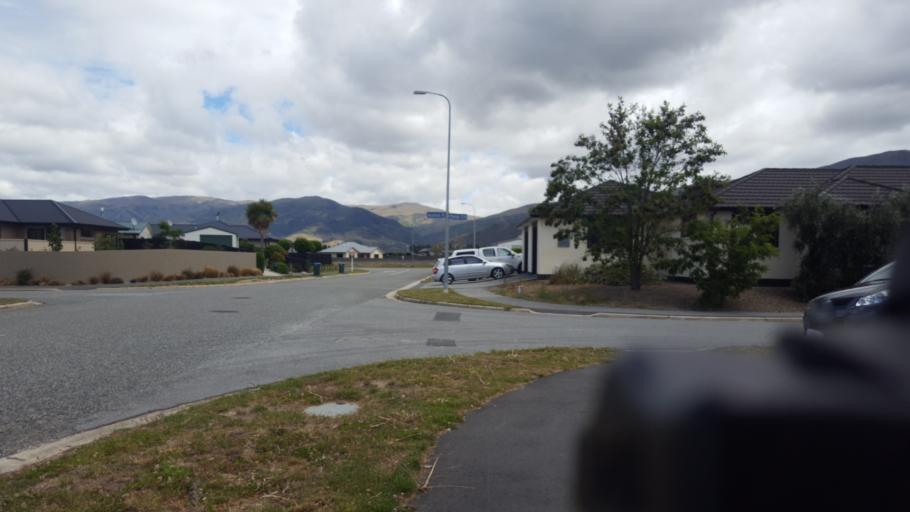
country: NZ
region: Otago
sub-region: Queenstown-Lakes District
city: Wanaka
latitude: -45.0439
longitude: 169.1815
